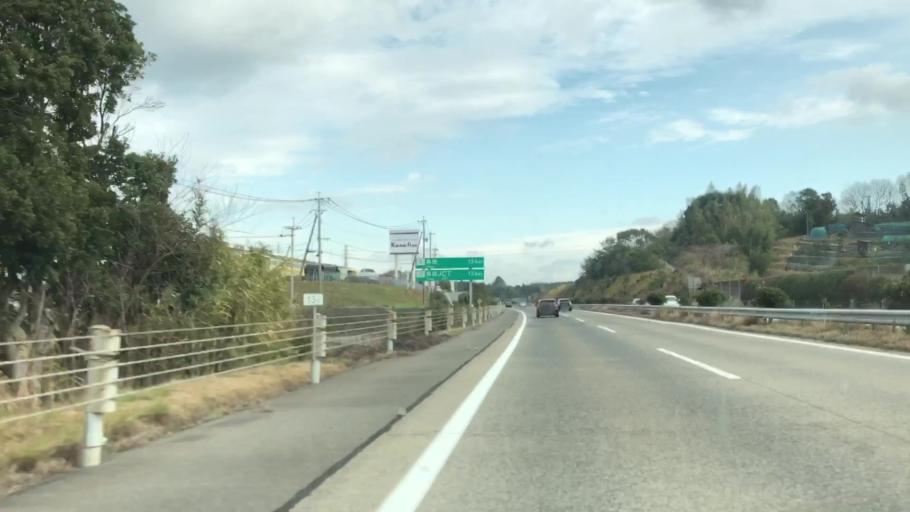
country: JP
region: Saga Prefecture
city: Kanzakimachi-kanzaki
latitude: 33.3542
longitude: 130.4107
